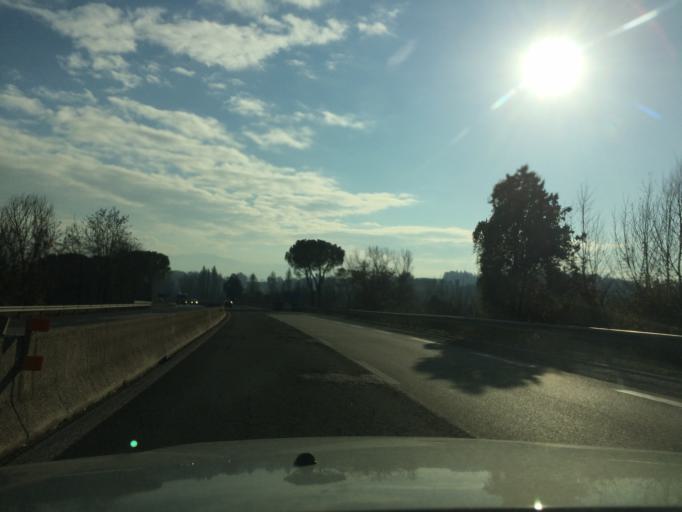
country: IT
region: Umbria
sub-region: Provincia di Terni
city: San Gemini
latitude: 42.5952
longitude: 12.5631
